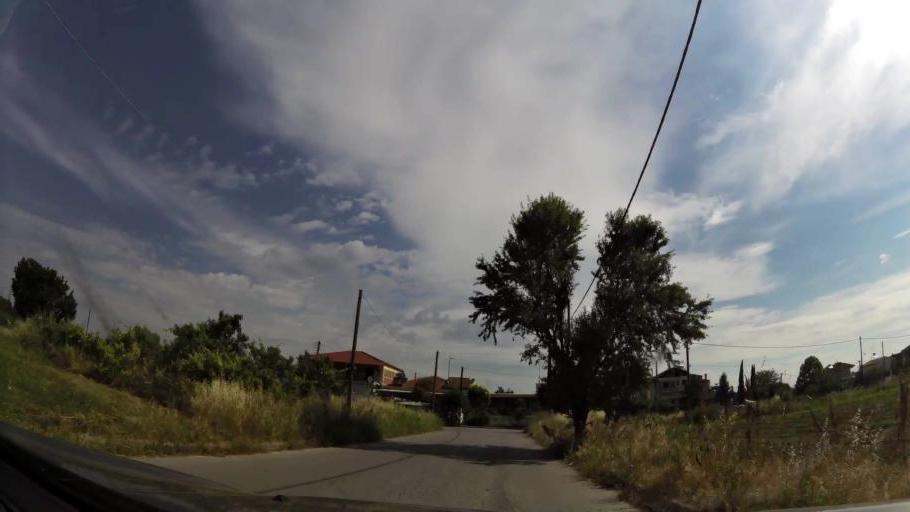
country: GR
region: Central Macedonia
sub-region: Nomos Pierias
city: Katerini
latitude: 40.2824
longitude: 22.4967
